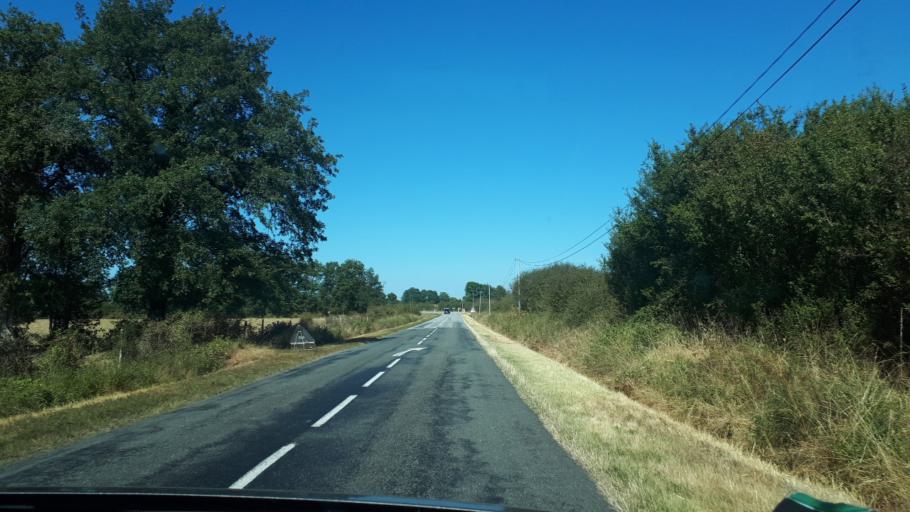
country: FR
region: Centre
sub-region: Departement du Loiret
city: Coullons
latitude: 47.6370
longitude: 2.4473
